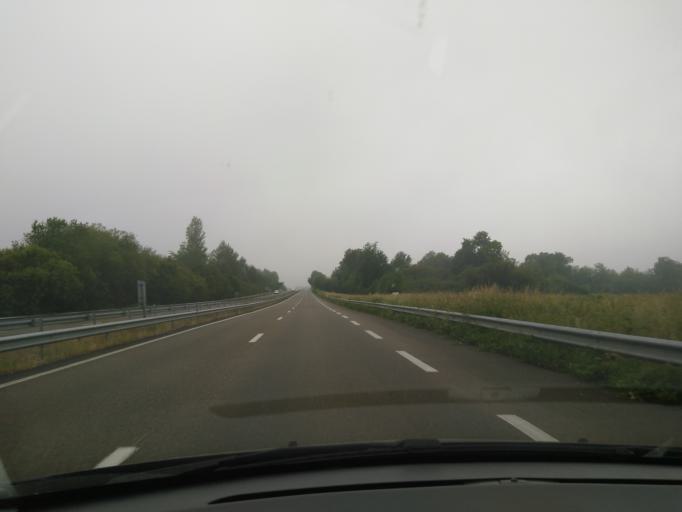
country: FR
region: Aquitaine
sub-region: Departement des Landes
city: Meilhan
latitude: 43.8644
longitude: -0.6785
